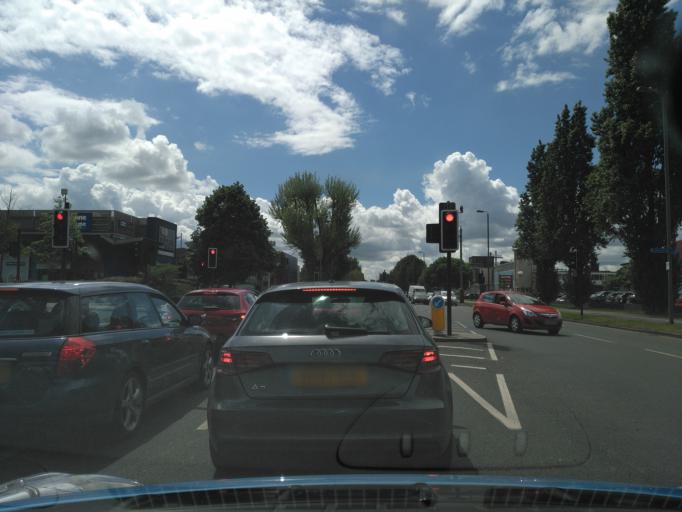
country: GB
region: England
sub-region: Greater London
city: Orpington
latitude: 51.3936
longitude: 0.1116
